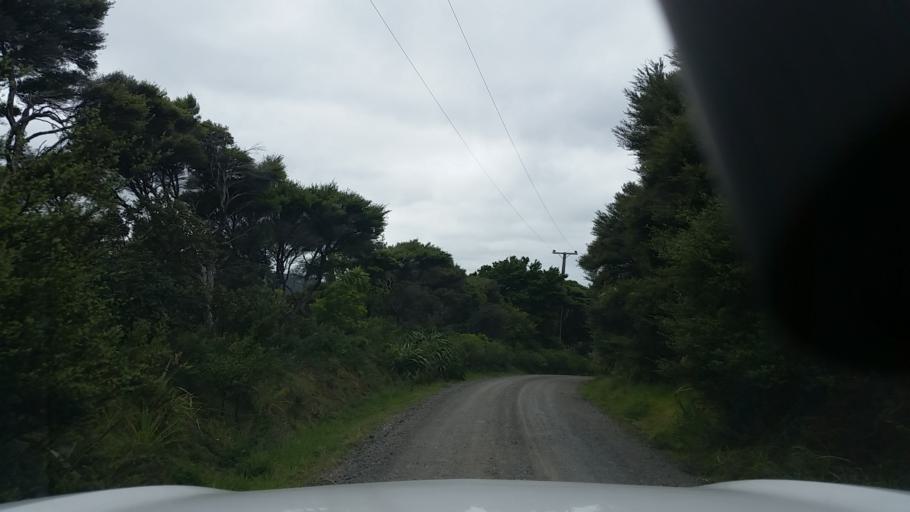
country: NZ
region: Auckland
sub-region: Auckland
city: Muriwai Beach
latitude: -36.8768
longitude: 174.4649
